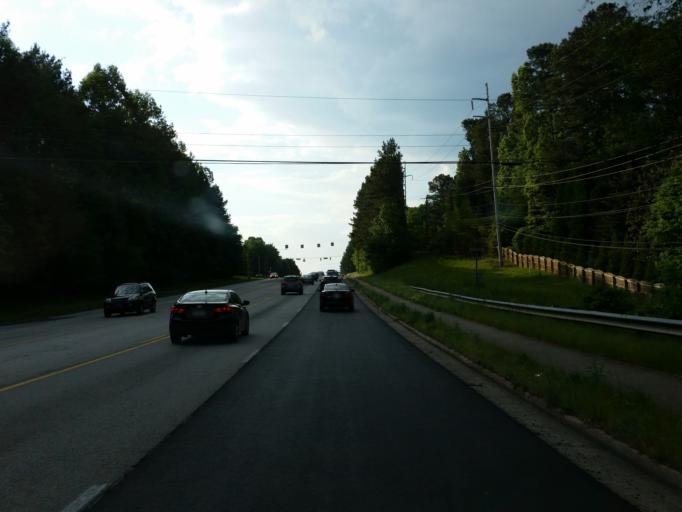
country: US
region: Georgia
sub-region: Cobb County
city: Smyrna
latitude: 33.8505
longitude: -84.5084
